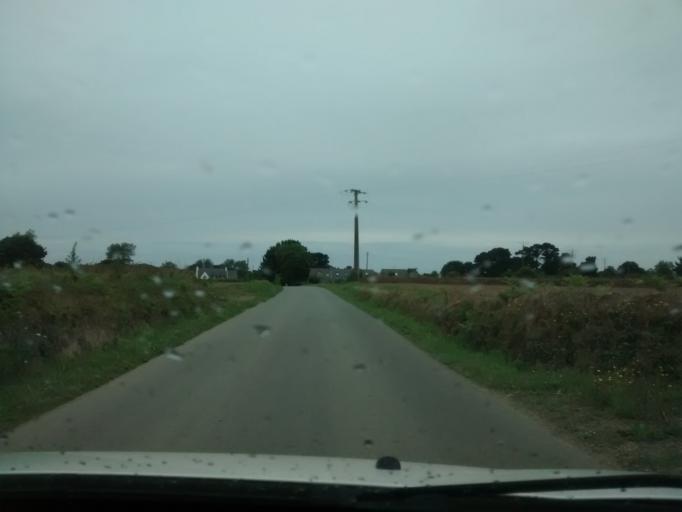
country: FR
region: Brittany
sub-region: Departement des Cotes-d'Armor
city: Penvenan
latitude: 48.8189
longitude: -3.3038
